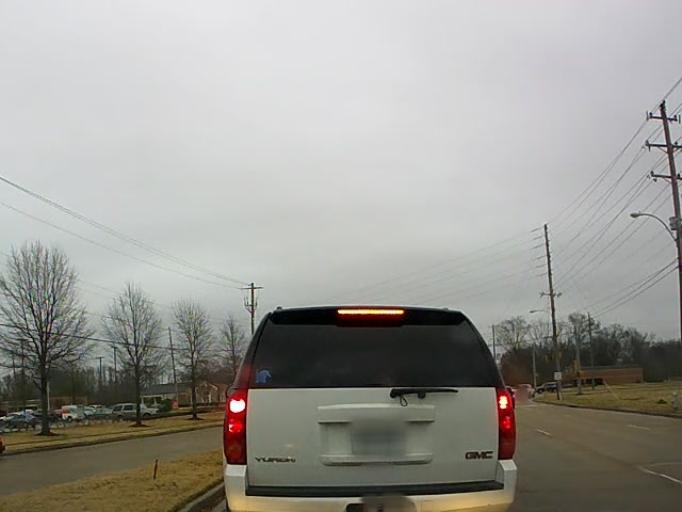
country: US
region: Tennessee
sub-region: Shelby County
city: Collierville
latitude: 35.0471
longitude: -89.7339
